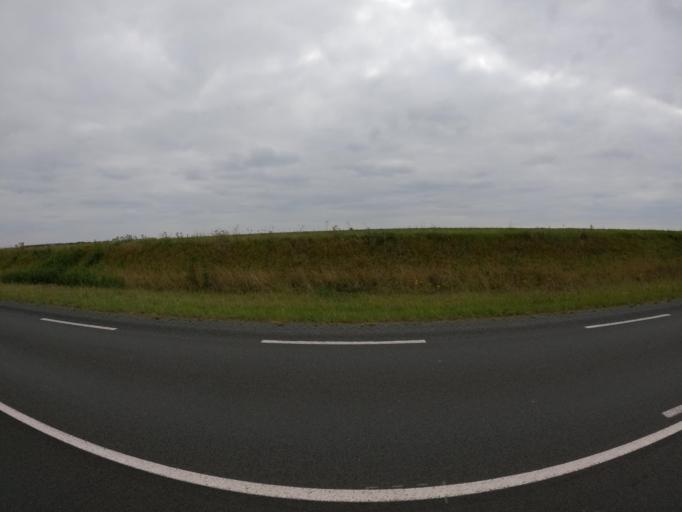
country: FR
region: Pays de la Loire
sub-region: Departement de la Vendee
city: Fontenay-le-Comte
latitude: 46.4429
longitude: -0.7979
